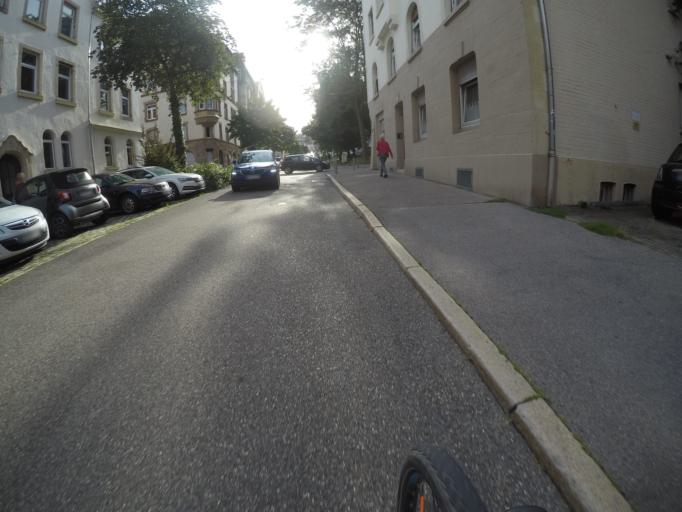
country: DE
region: Baden-Wuerttemberg
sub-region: Regierungsbezirk Stuttgart
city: Stuttgart
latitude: 48.7755
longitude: 9.1480
